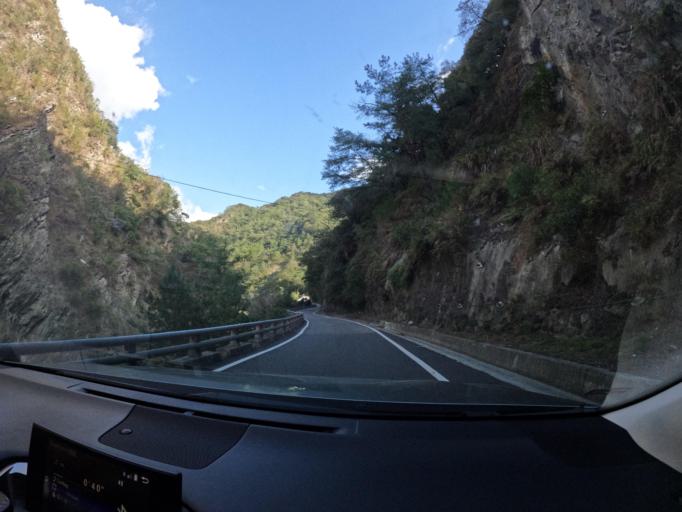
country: TW
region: Taiwan
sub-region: Taitung
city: Taitung
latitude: 23.1736
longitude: 121.0331
